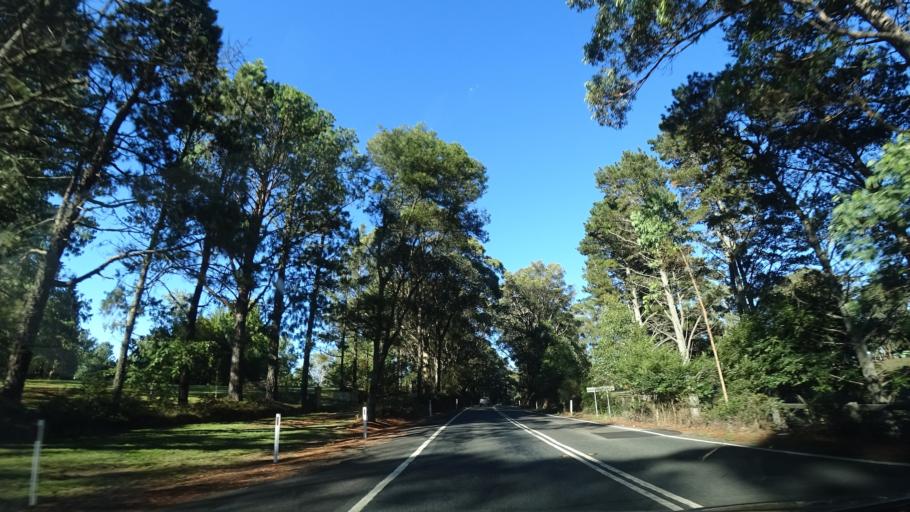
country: AU
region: New South Wales
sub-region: Blue Mountains Municipality
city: Lawson
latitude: -33.5183
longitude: 150.4658
